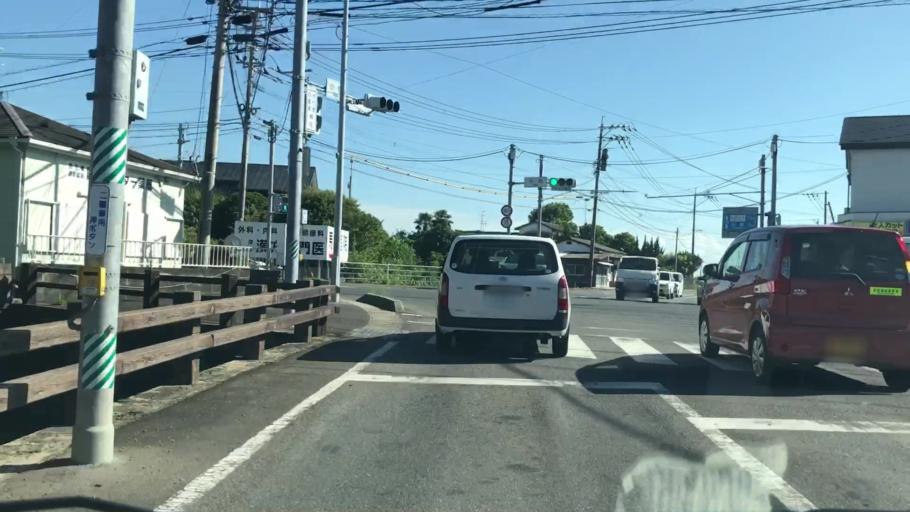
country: JP
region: Saga Prefecture
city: Okawa
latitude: 33.2237
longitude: 130.3517
